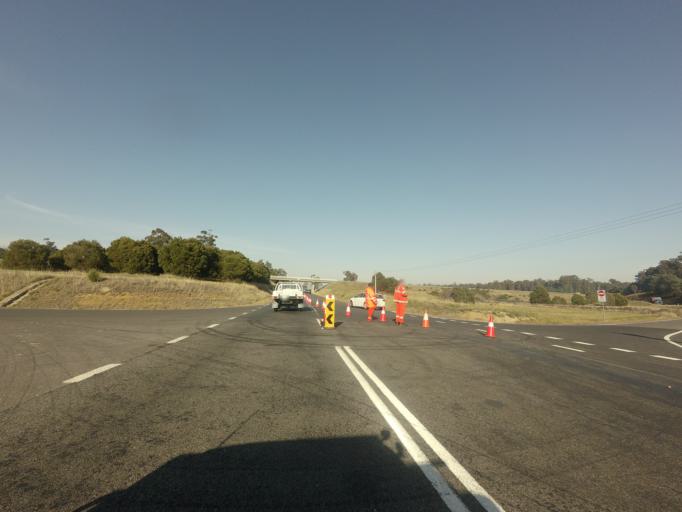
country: AU
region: Tasmania
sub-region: Northern Midlands
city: Longford
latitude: -41.5520
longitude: 146.9895
